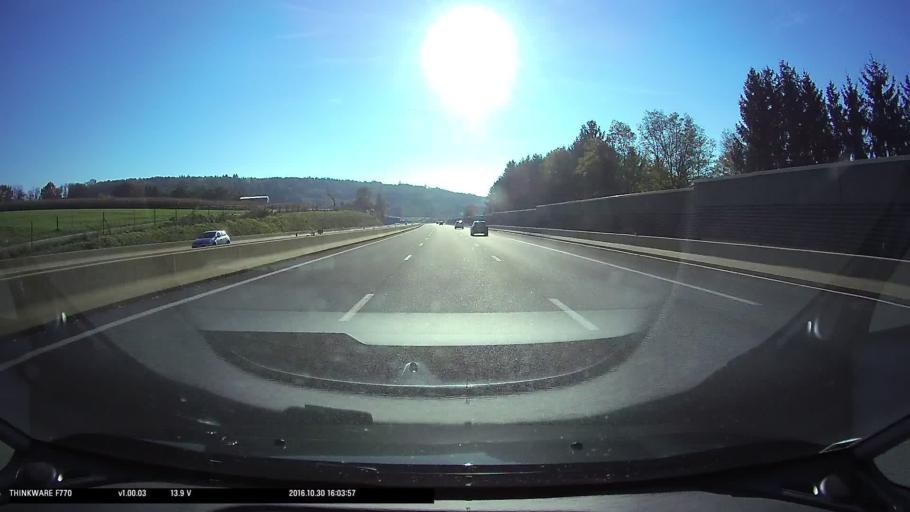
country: FR
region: Franche-Comte
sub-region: Departement du Doubs
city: Voujeaucourt
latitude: 47.4740
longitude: 6.7796
